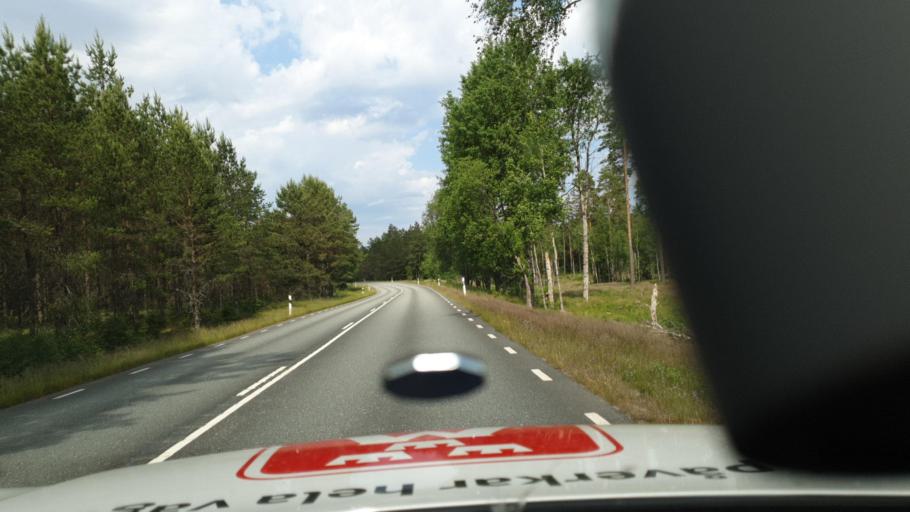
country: SE
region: Joenkoeping
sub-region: Varnamo Kommun
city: Varnamo
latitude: 57.2962
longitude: 14.0796
